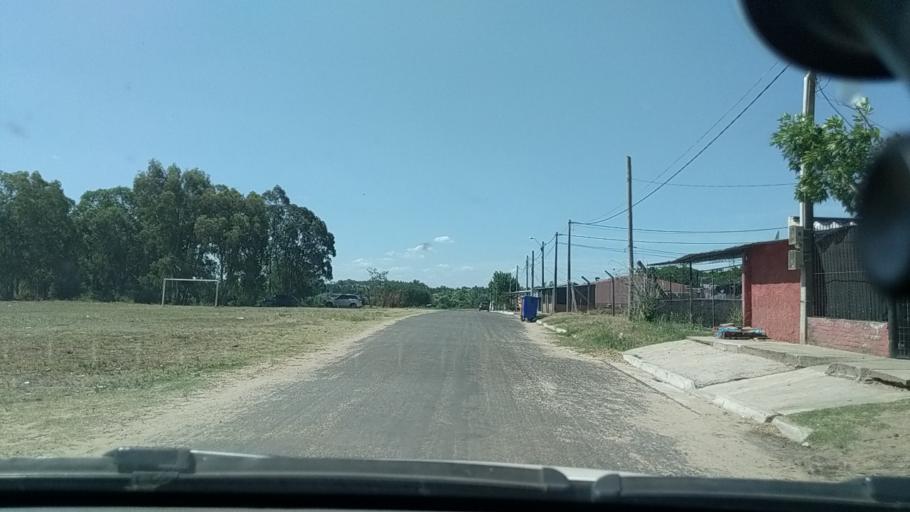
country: UY
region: Tacuarembo
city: Paso de los Toros
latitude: -32.8105
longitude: -56.5324
